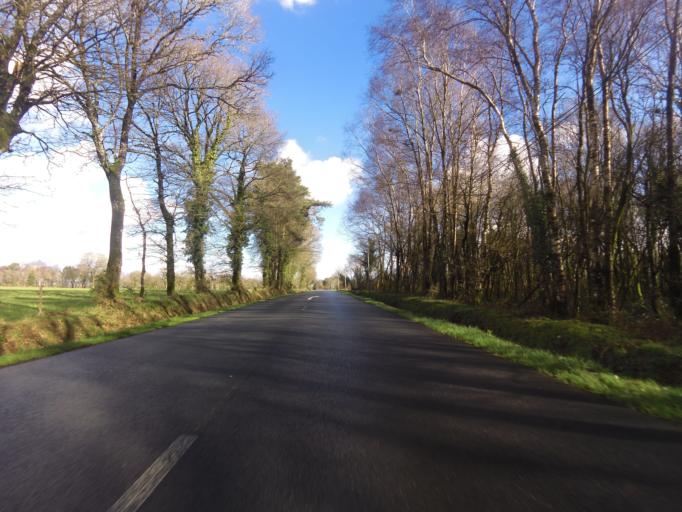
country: FR
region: Brittany
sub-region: Departement du Morbihan
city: Cleguerec
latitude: 48.0963
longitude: -3.0814
